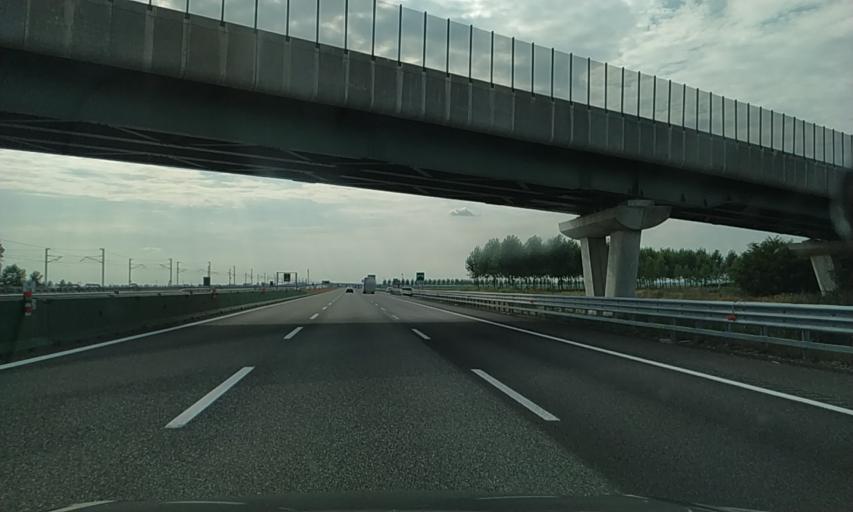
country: IT
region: Piedmont
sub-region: Provincia di Novara
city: San Pietro Mosezzo
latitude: 45.4709
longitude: 8.5237
